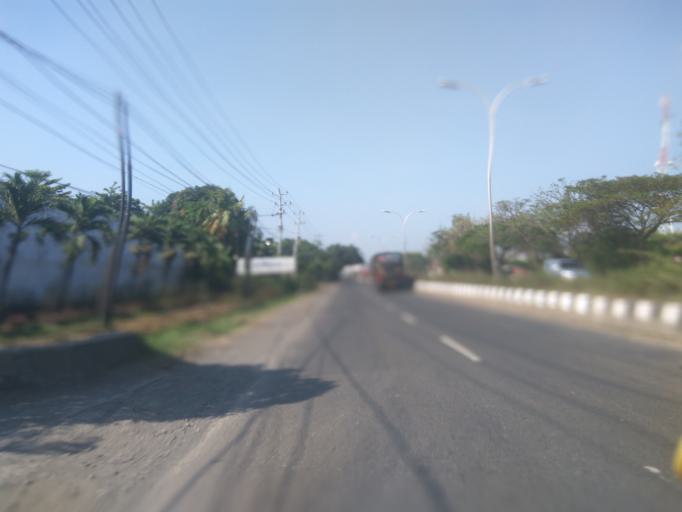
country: ID
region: Central Java
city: Semarang
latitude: -6.9491
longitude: 110.4866
